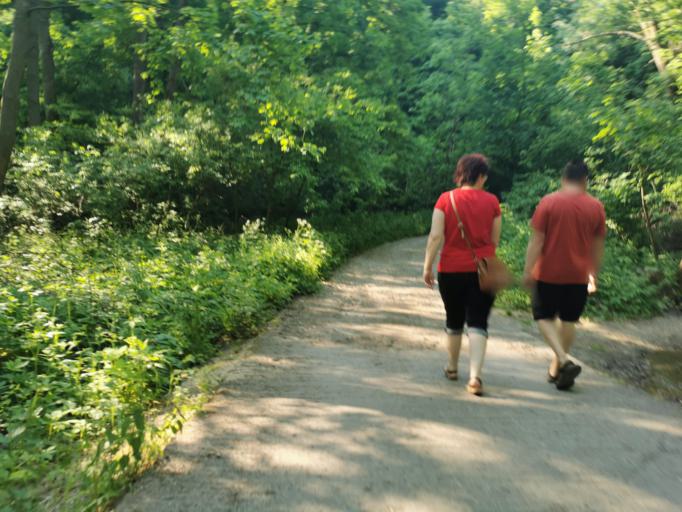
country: CZ
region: South Moravian
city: Knezdub
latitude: 48.8667
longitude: 17.4056
